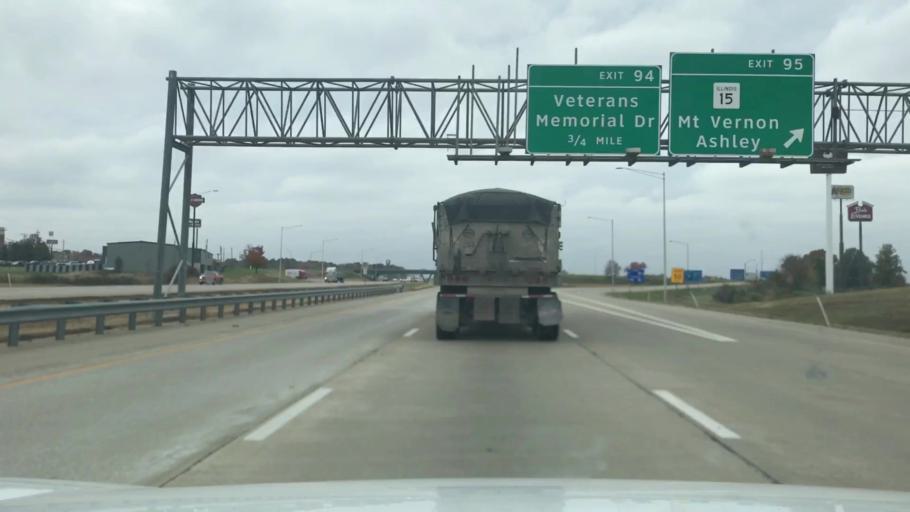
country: US
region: Illinois
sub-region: Jefferson County
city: Mount Vernon
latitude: 38.3174
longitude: -88.9541
